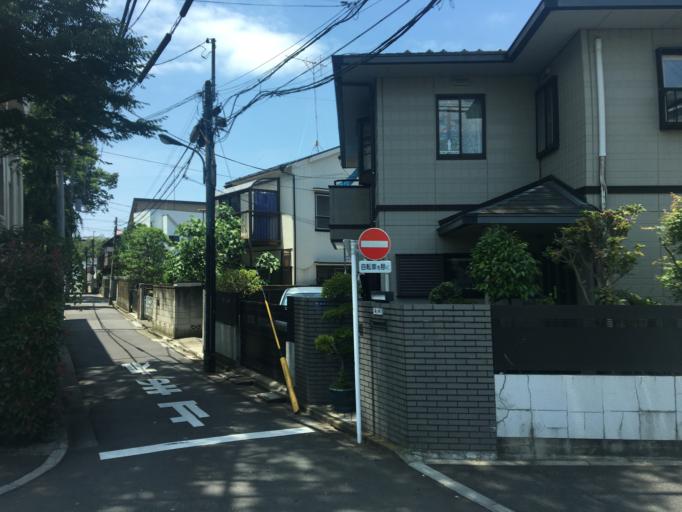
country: JP
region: Saitama
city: Kawaguchi
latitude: 35.7792
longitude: 139.7137
